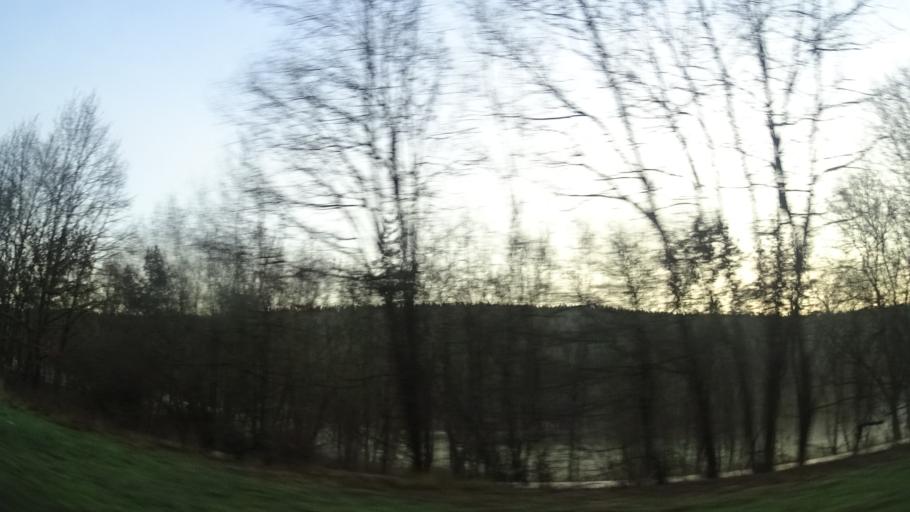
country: DE
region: Bavaria
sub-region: Regierungsbezirk Unterfranken
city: Hohenroth
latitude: 50.3507
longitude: 10.1566
